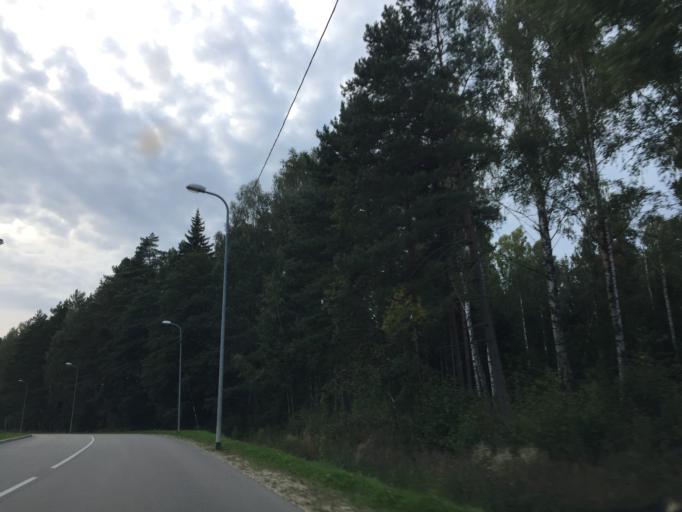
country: LV
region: Saulkrastu
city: Saulkrasti
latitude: 57.3233
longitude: 24.4163
